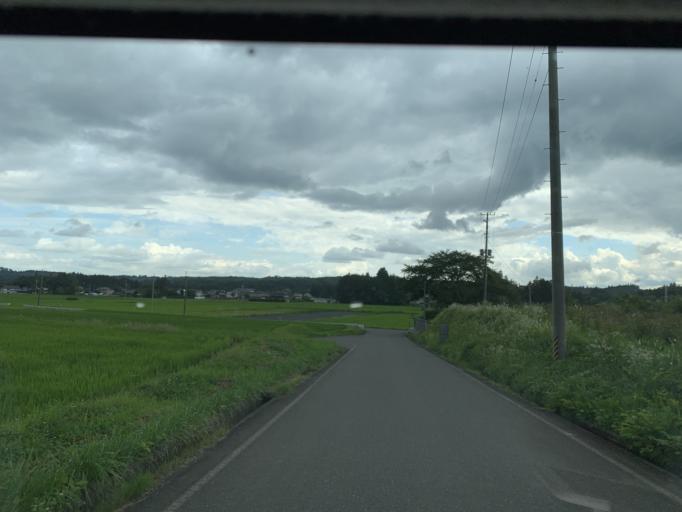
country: JP
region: Iwate
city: Ichinoseki
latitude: 38.9520
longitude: 141.0474
